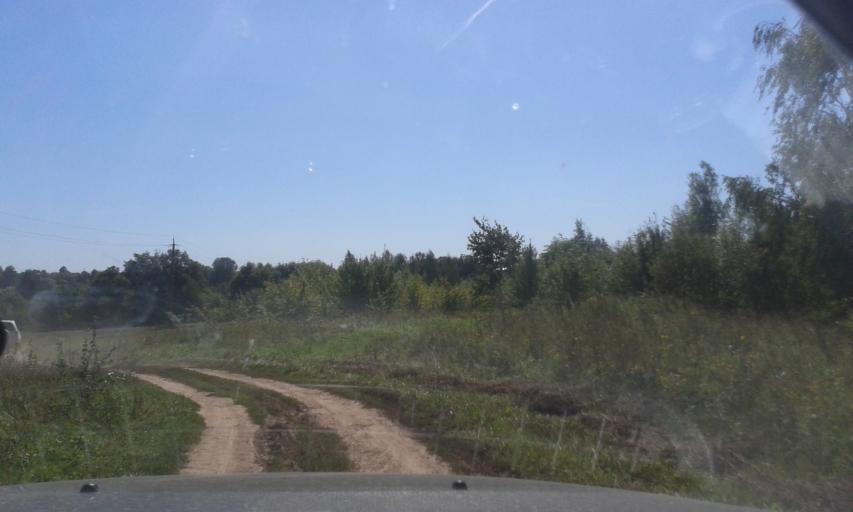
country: RU
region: Tula
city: Dubna
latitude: 54.1406
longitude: 37.1586
